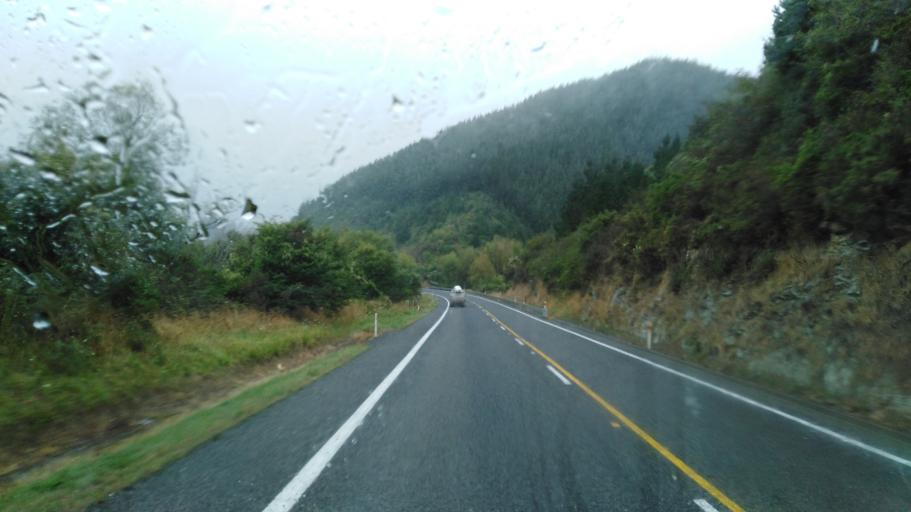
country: NZ
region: Marlborough
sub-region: Marlborough District
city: Picton
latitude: -41.3878
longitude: 173.9519
